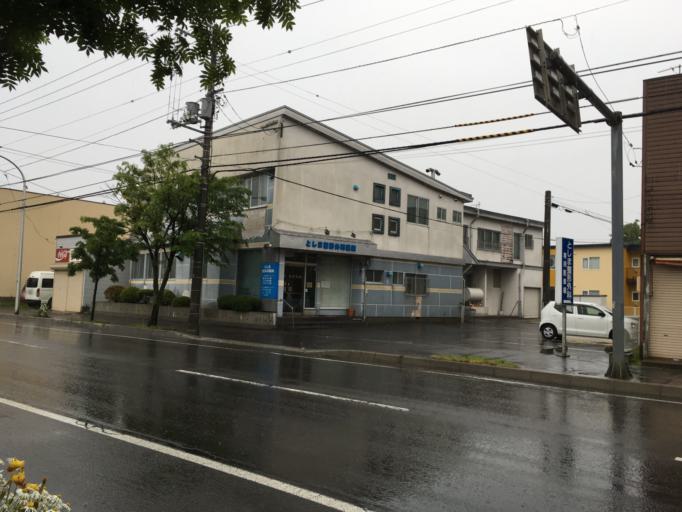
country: JP
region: Hokkaido
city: Hakodate
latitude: 41.7790
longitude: 140.7354
